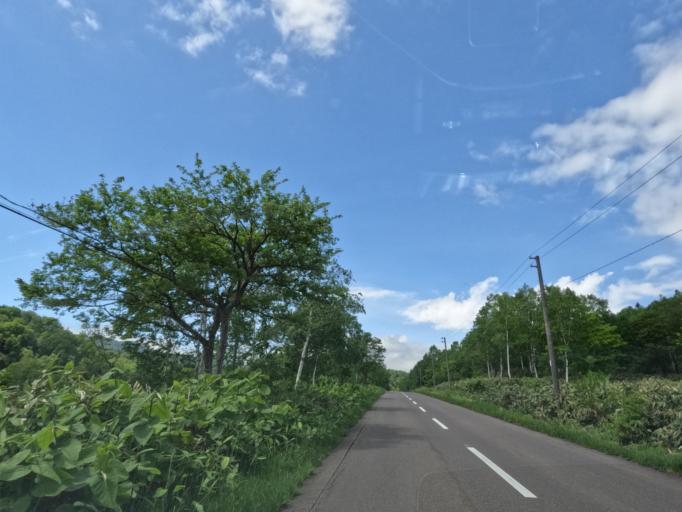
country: JP
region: Hokkaido
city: Tobetsu
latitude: 43.5123
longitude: 141.5917
